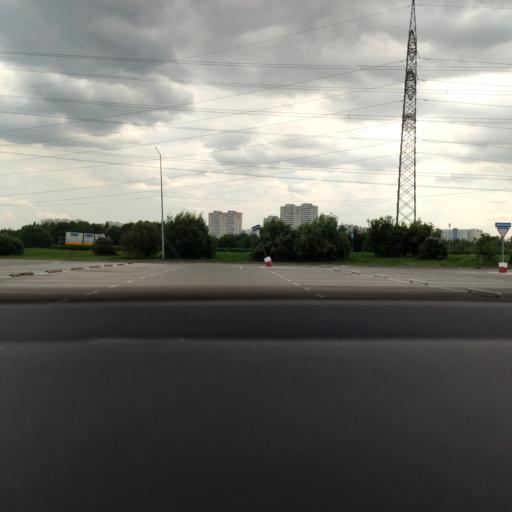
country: RU
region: Moscow
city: Lianozovo
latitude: 55.9123
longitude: 37.5738
